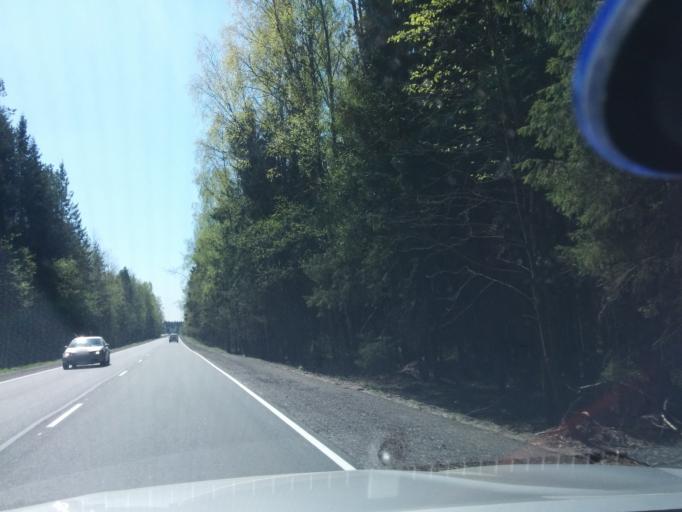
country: RU
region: Leningrad
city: Verkhniye Osel'ki
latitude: 60.2097
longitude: 30.4264
